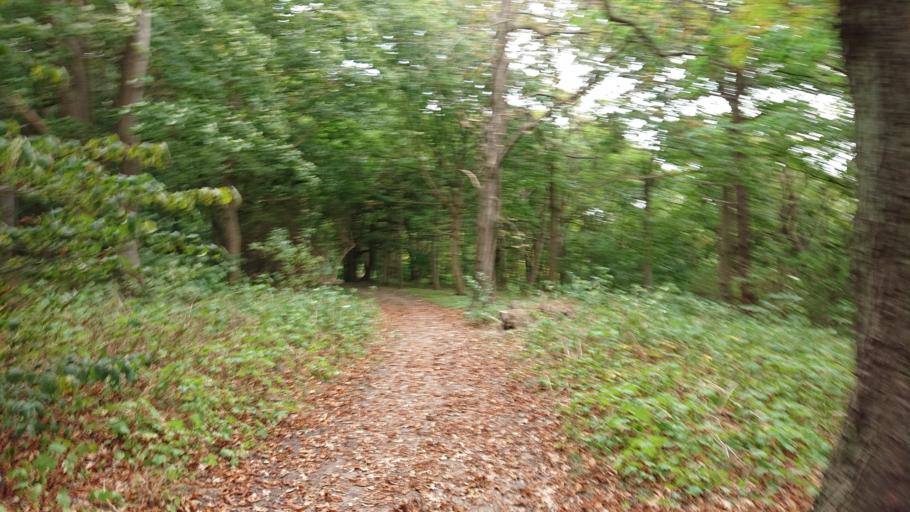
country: DE
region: Mecklenburg-Vorpommern
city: Altefahr
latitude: 54.3330
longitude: 13.1152
